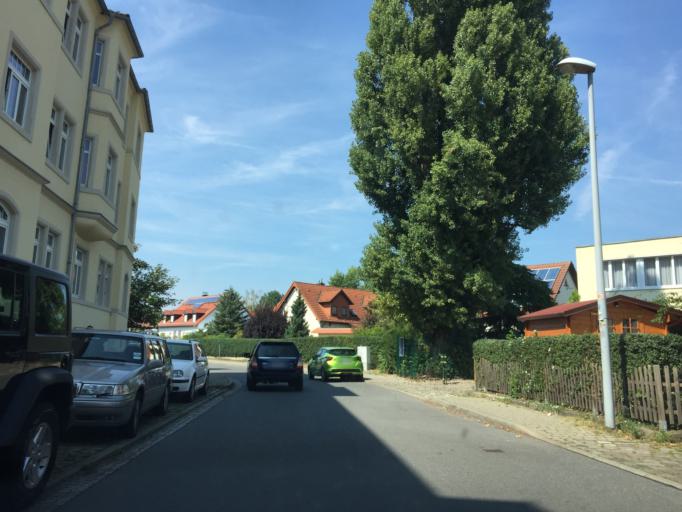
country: DE
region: Saxony
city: Dresden
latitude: 51.0745
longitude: 13.7016
